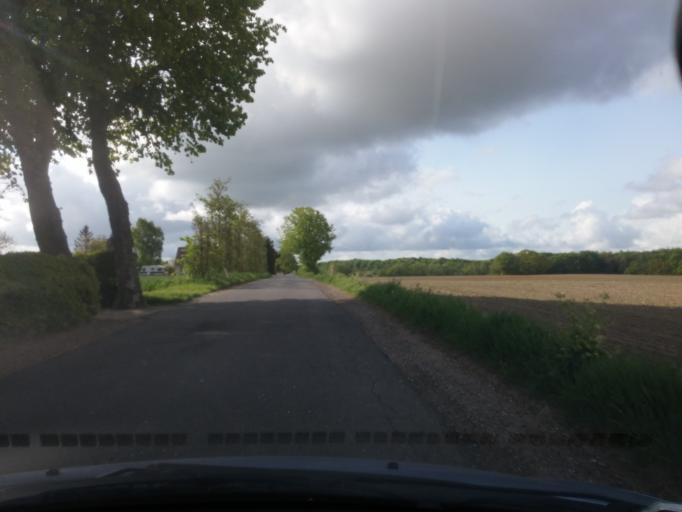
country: DK
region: South Denmark
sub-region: Nyborg Kommune
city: Ullerslev
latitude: 55.3842
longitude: 10.6401
